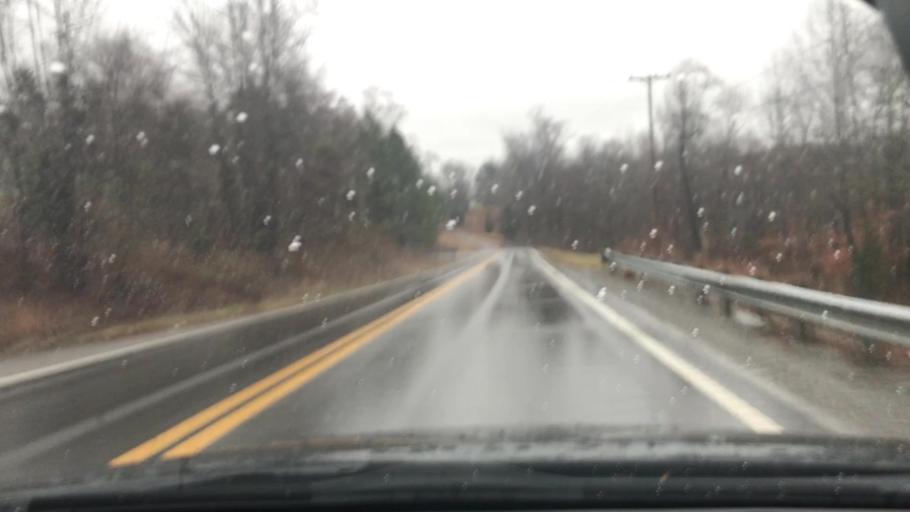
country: US
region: Tennessee
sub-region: Cheatham County
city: Ashland City
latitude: 36.2799
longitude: -87.1134
